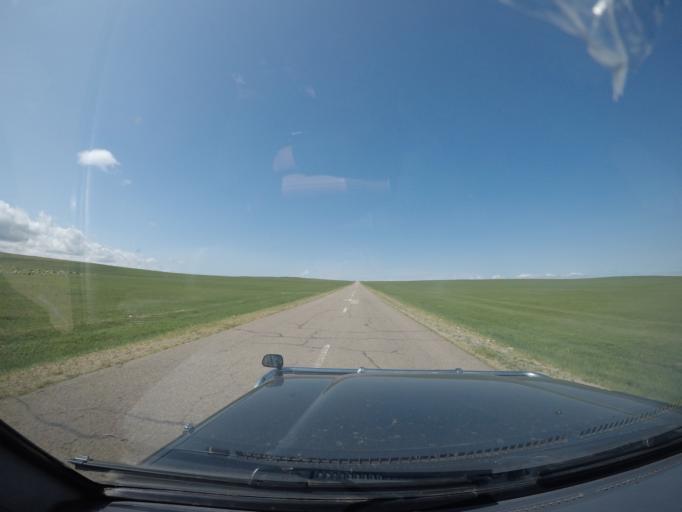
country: MN
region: Hentiy
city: Bayan
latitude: 47.2834
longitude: 110.9454
